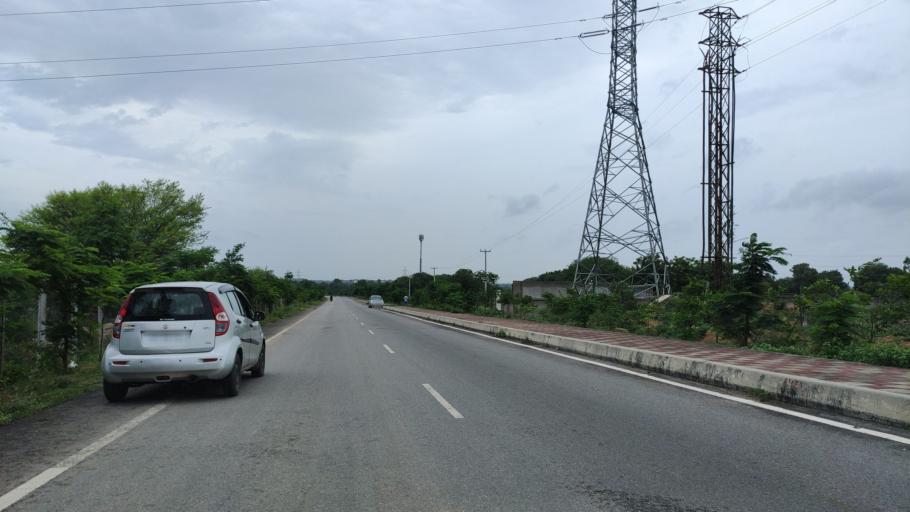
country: IN
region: Telangana
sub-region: Rangareddi
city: Secunderabad
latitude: 17.5778
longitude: 78.5979
